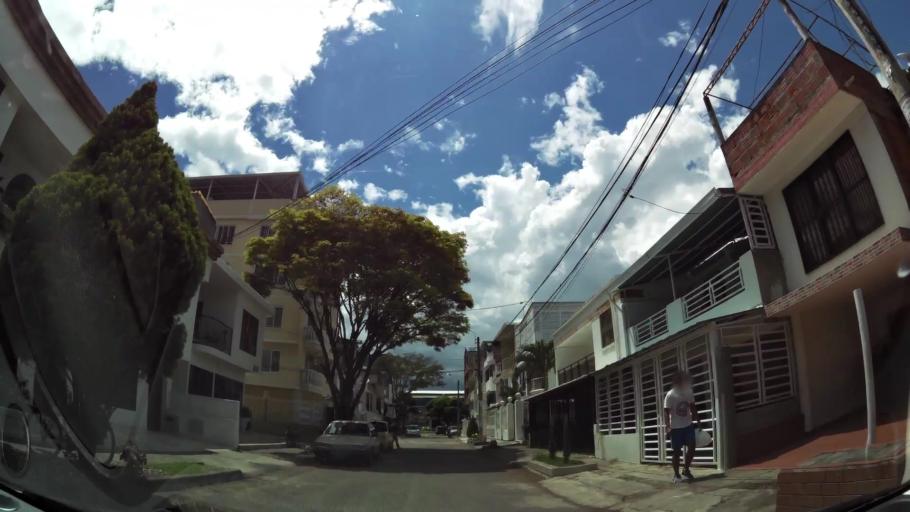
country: CO
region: Valle del Cauca
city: Cali
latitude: 3.3877
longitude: -76.5191
